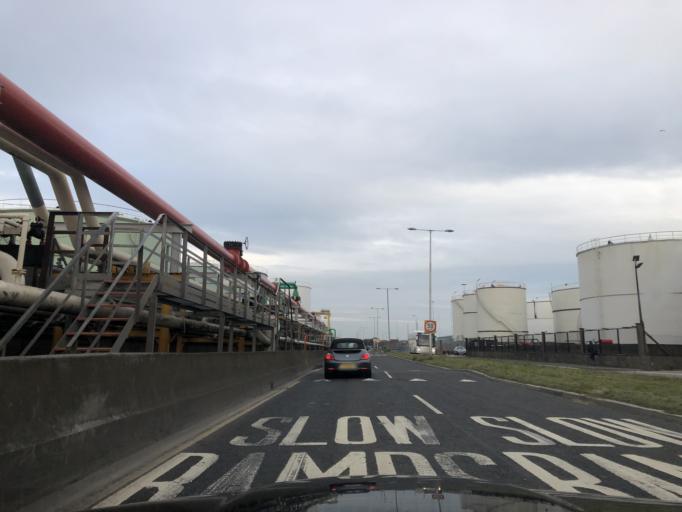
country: IE
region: Leinster
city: Sandymount
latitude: 53.3515
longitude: -6.2055
